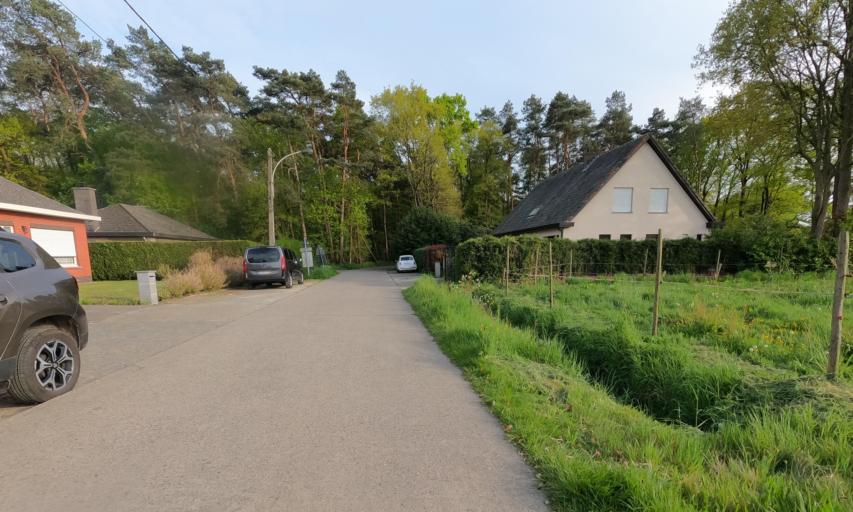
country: BE
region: Flanders
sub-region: Provincie Antwerpen
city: Zandhoven
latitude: 51.2568
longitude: 4.6539
